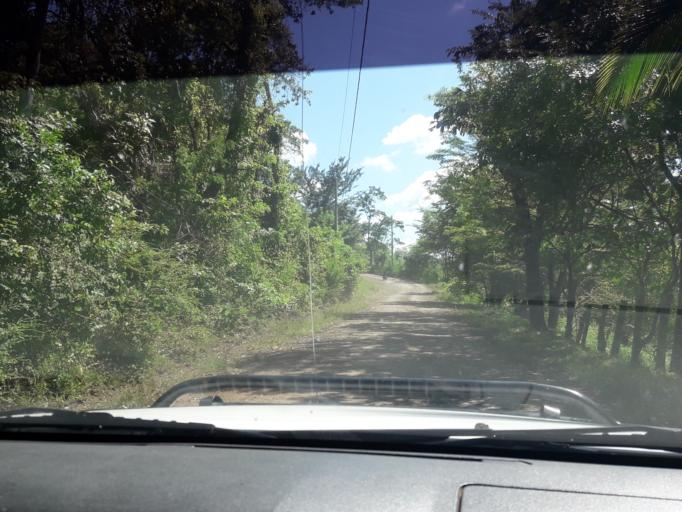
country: NI
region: Rivas
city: Cardenas
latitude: 11.2237
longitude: -85.6501
